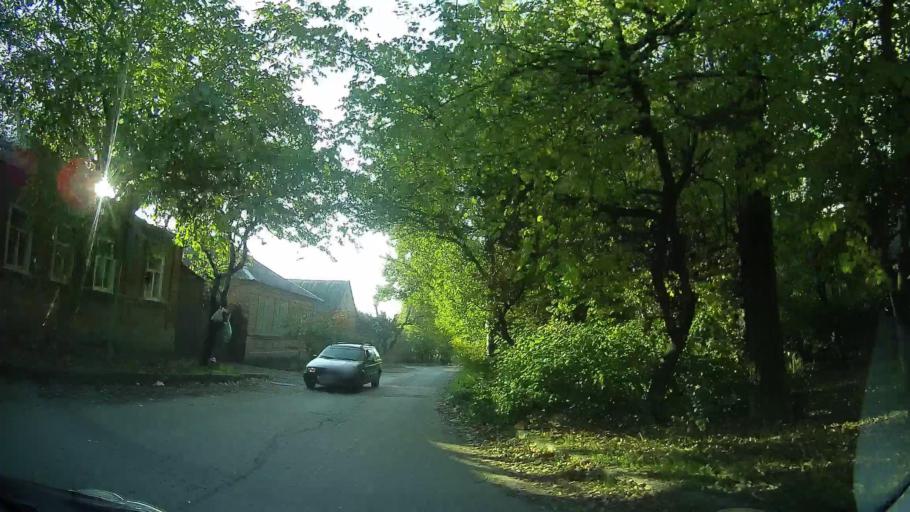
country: RU
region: Rostov
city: Severnyy
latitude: 47.2692
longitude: 39.6727
